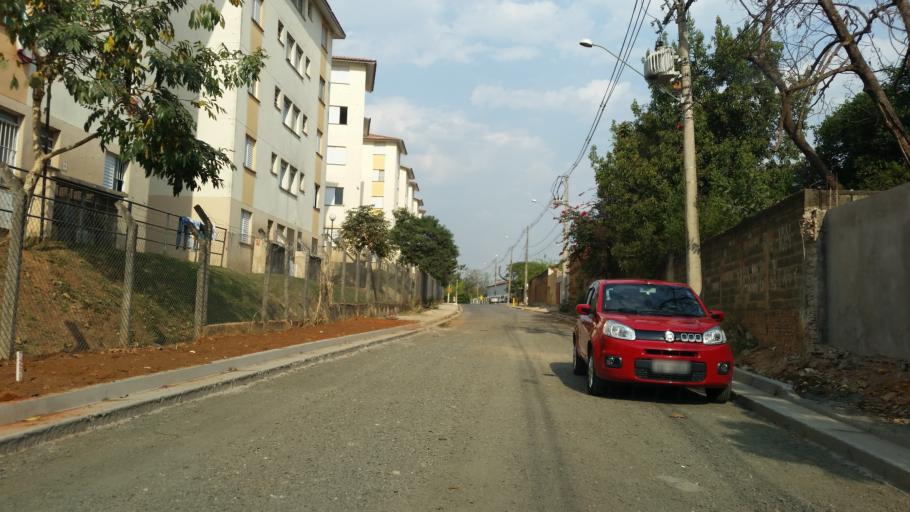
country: BR
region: Sao Paulo
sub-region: Hortolandia
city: Hortolandia
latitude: -22.8807
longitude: -47.1771
